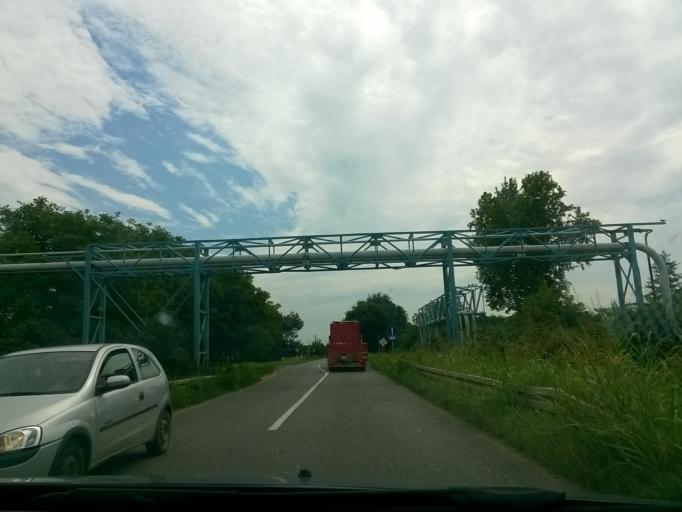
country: RS
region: Autonomna Pokrajina Vojvodina
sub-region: Srednjebanatski Okrug
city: Zrenjanin
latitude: 45.3852
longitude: 20.4265
